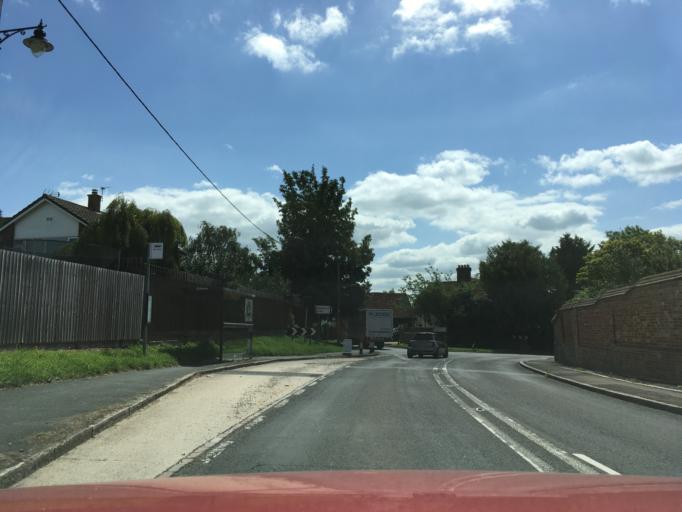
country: GB
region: England
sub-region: Buckinghamshire
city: Aylesbury
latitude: 51.8769
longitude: -0.8321
